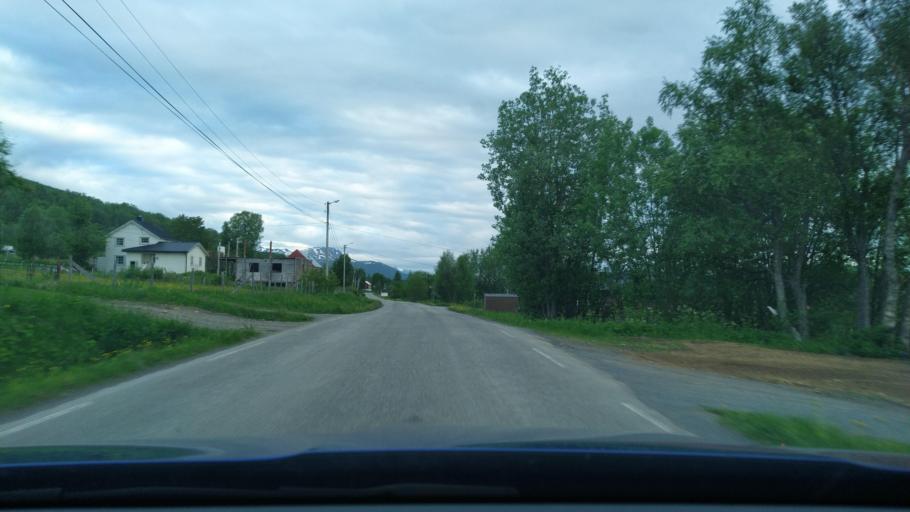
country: NO
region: Troms
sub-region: Tranoy
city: Vangsvika
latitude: 69.1170
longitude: 17.8008
